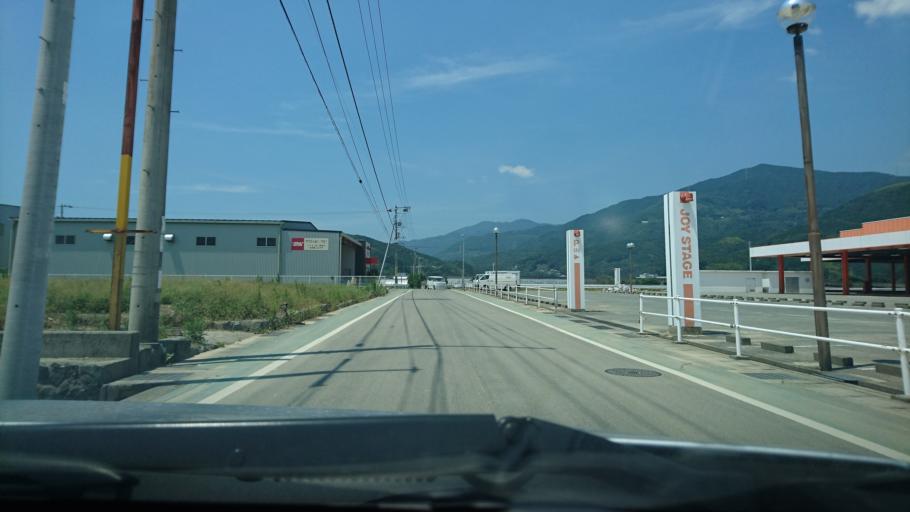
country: JP
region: Ehime
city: Ozu
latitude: 33.5299
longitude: 132.5686
